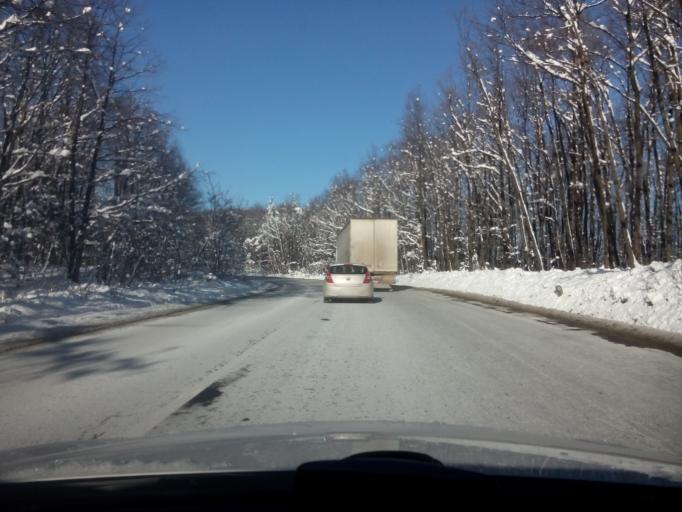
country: RO
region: Arges
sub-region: Comuna Cotmeana
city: Cotmeana
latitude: 44.9763
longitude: 24.6633
